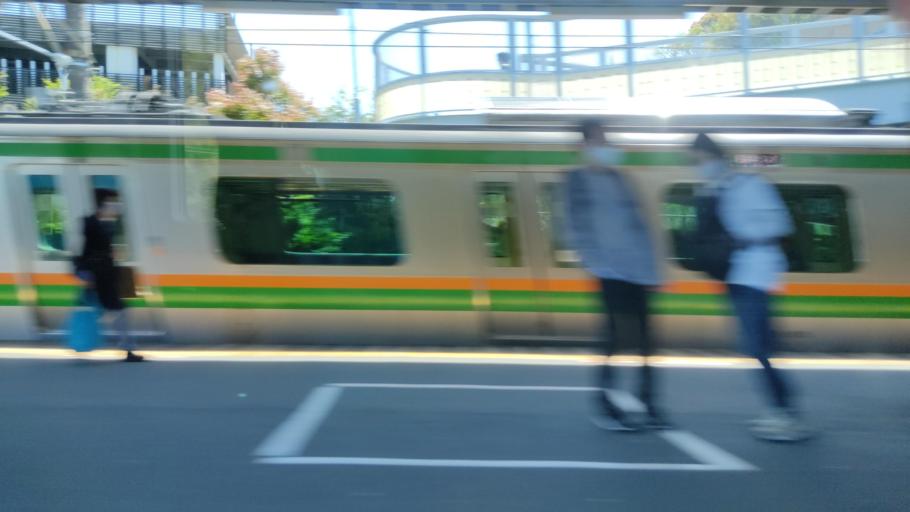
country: JP
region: Kanagawa
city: Oiso
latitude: 35.3116
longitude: 139.3138
